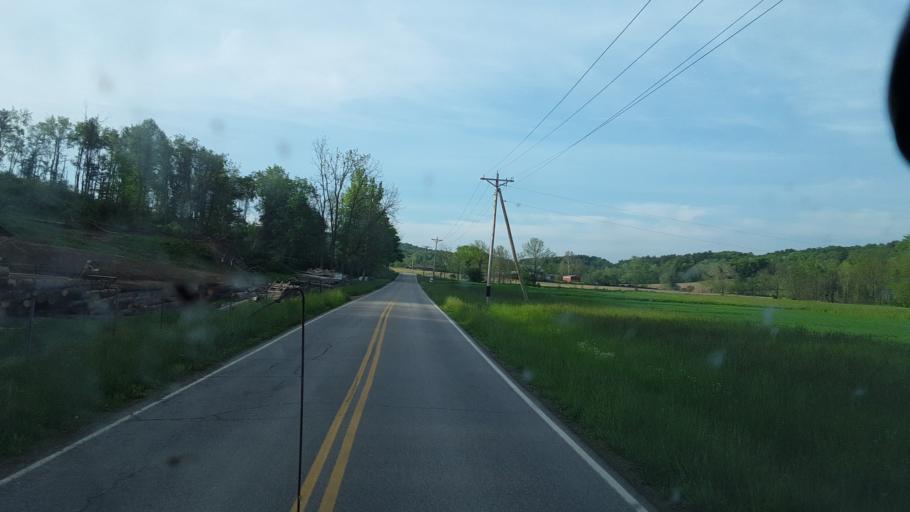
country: US
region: Ohio
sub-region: Fairfield County
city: Lancaster
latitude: 39.5176
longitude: -82.6952
